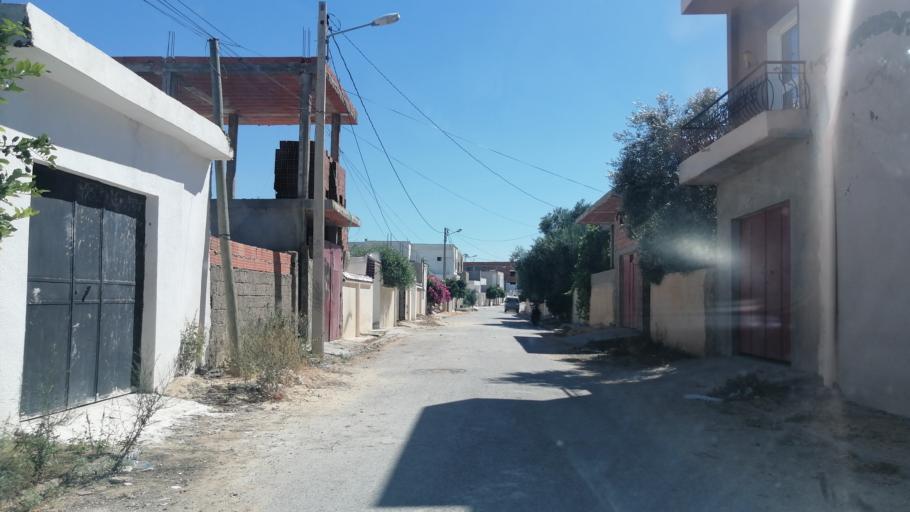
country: TN
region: Al Qayrawan
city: Sbikha
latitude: 36.1270
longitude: 10.0958
